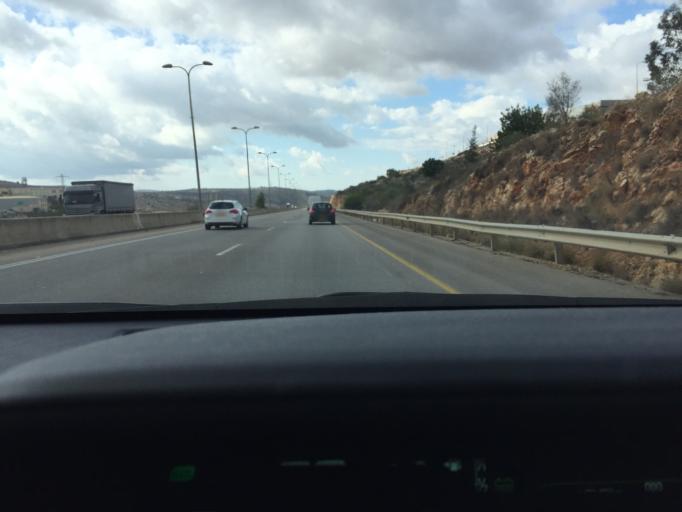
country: IL
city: Revava
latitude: 32.1009
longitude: 35.1225
